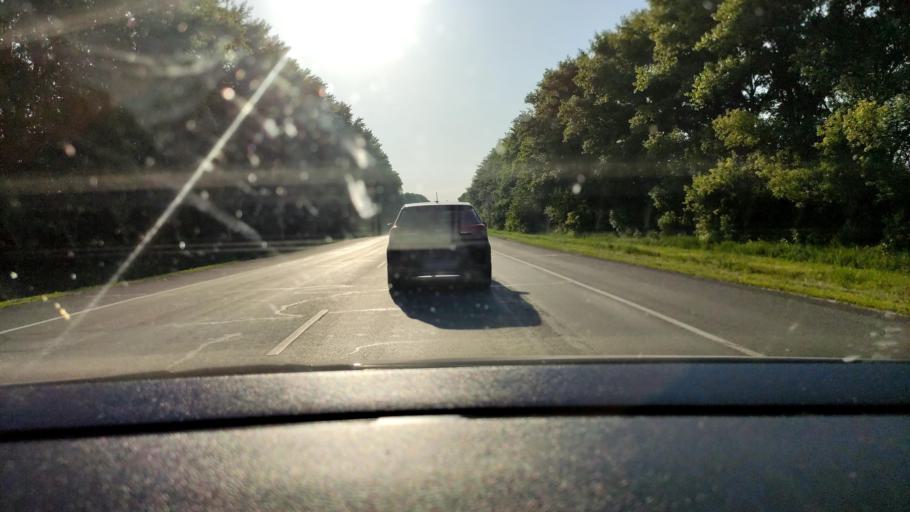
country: RU
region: Voronezj
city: Kashirskoye
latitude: 51.4947
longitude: 39.6007
